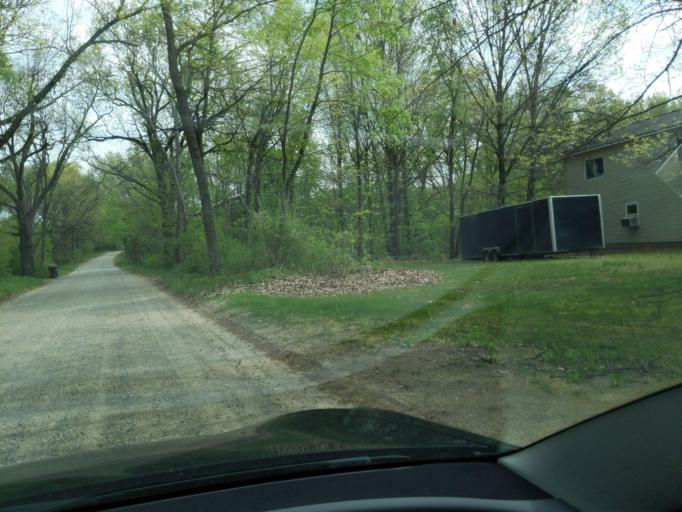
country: US
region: Michigan
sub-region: Washtenaw County
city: Chelsea
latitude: 42.4197
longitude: -84.0622
